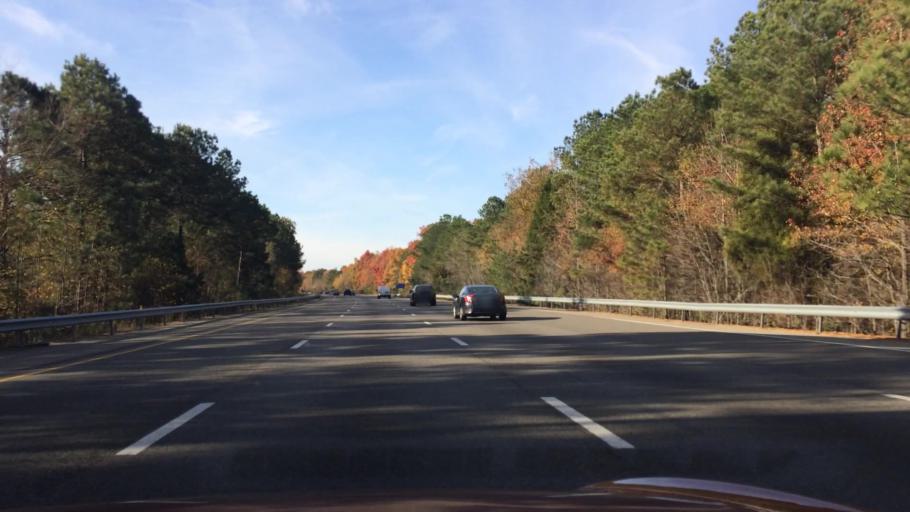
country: US
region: Virginia
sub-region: Henrico County
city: Short Pump
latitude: 37.6684
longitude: -77.5889
